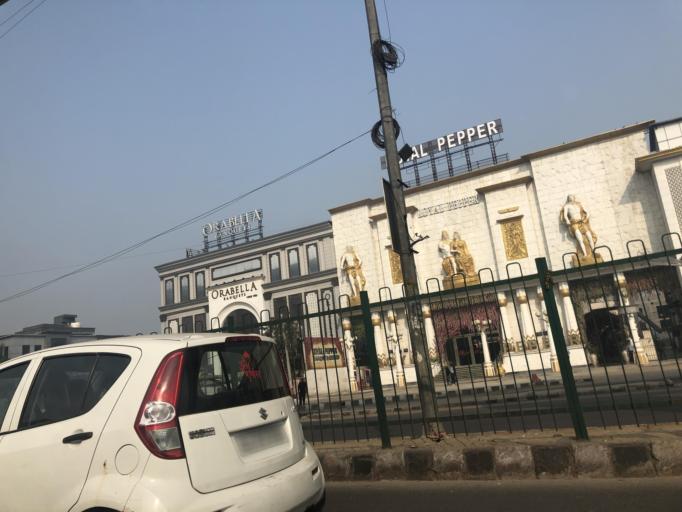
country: IN
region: NCT
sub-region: West Delhi
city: Nangloi Jat
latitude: 28.6796
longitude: 77.0940
